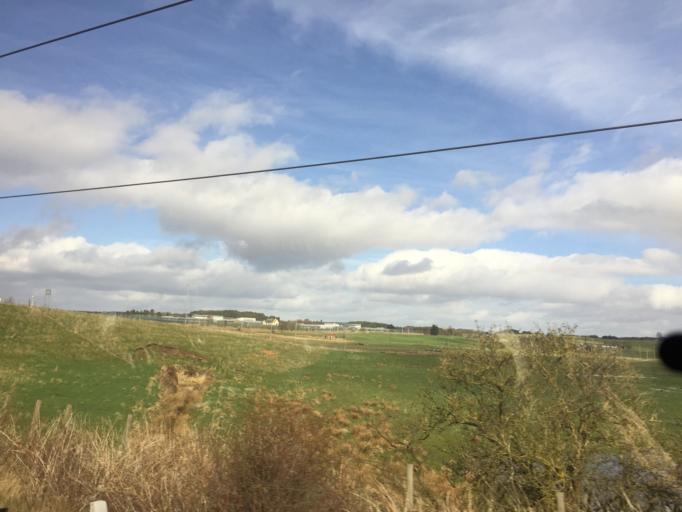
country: GB
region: Scotland
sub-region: South Lanarkshire
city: Carnwath
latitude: 55.6863
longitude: -3.6591
